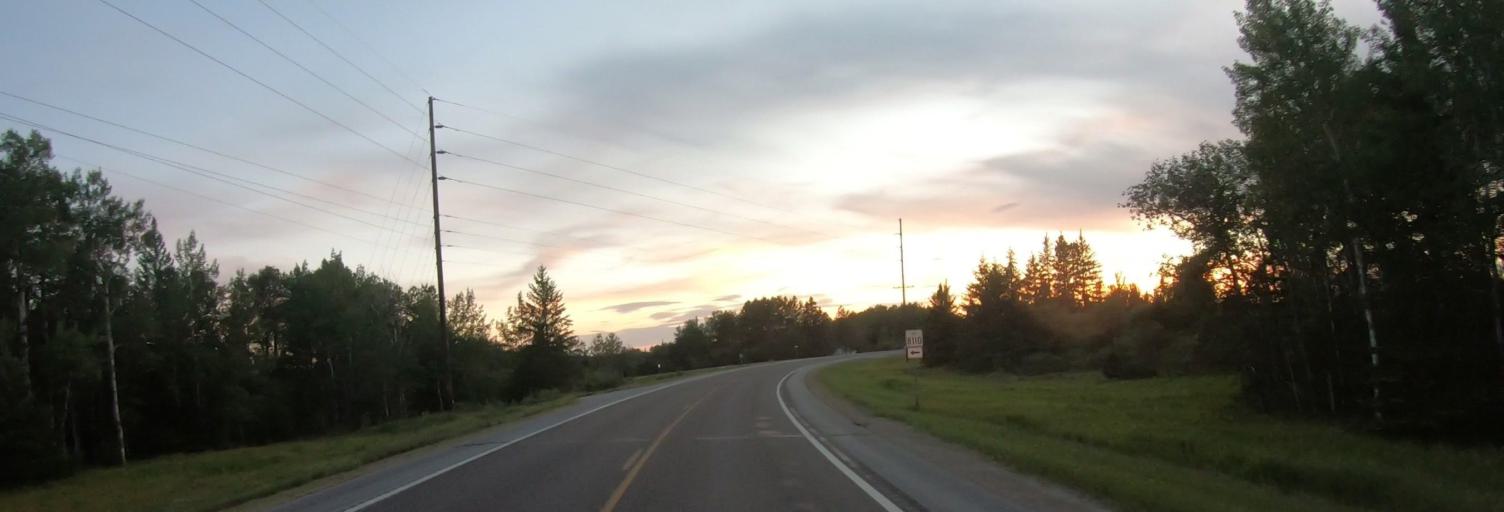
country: US
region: Minnesota
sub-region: Saint Louis County
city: Parkville
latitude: 47.8450
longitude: -92.5261
